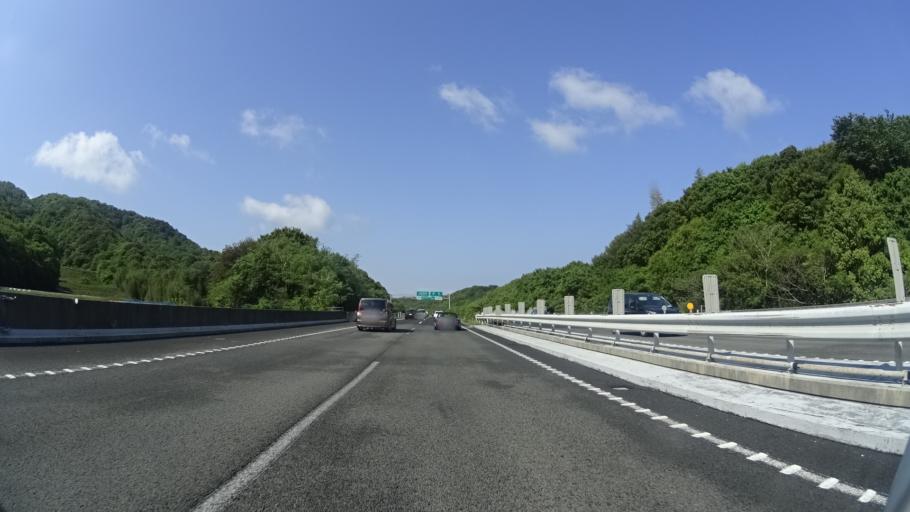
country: JP
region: Hyogo
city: Fukura
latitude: 34.2756
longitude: 134.7020
